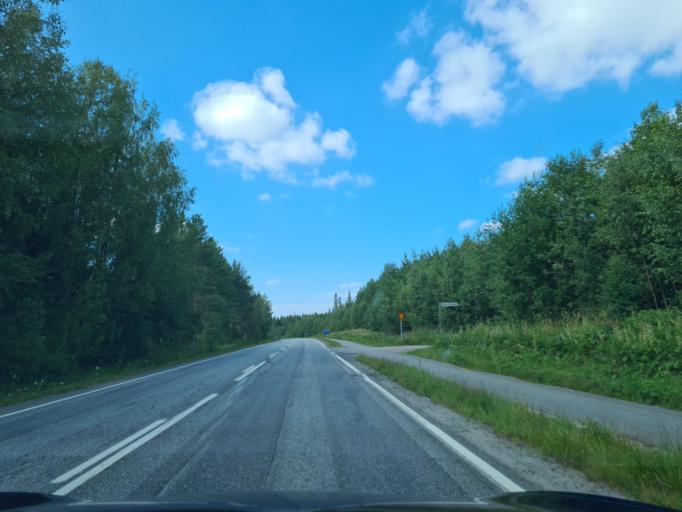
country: FI
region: Ostrobothnia
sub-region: Vaasa
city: Replot
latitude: 63.2021
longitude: 21.5295
